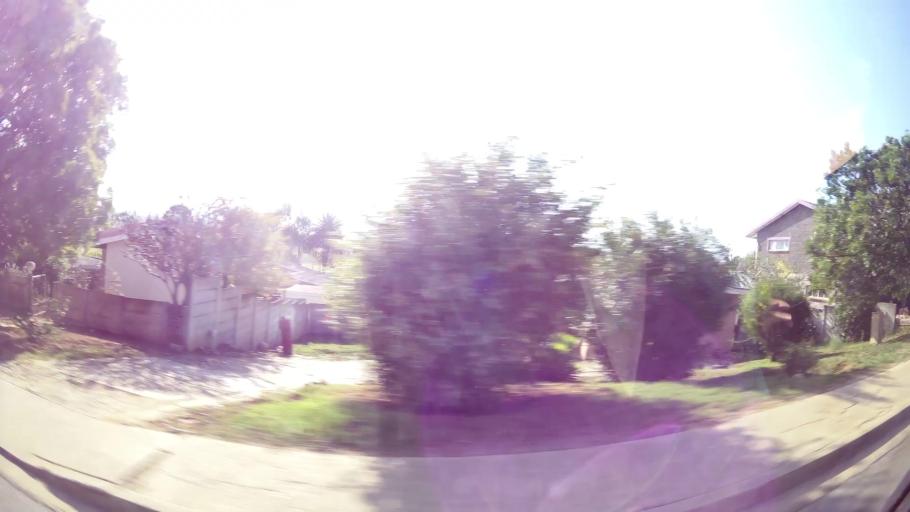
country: ZA
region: Eastern Cape
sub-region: Nelson Mandela Bay Metropolitan Municipality
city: Uitenhage
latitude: -33.7700
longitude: 25.4191
